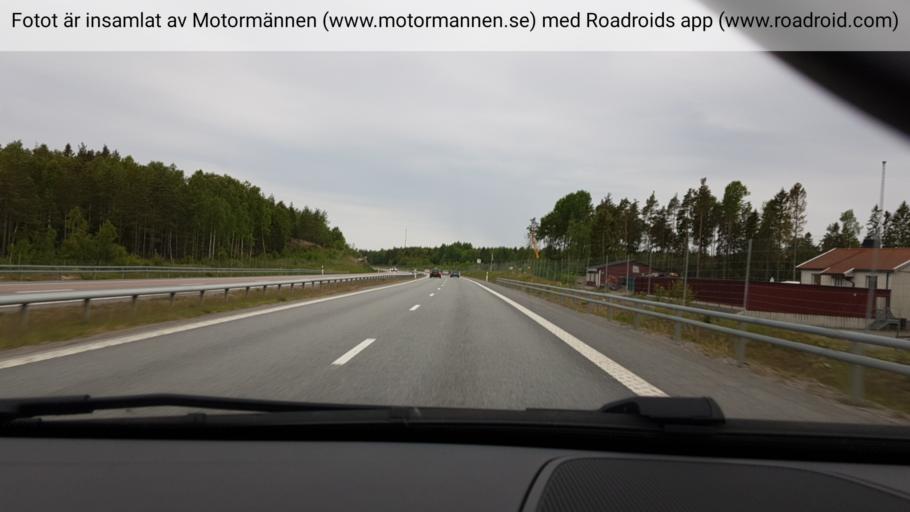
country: SE
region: Stockholm
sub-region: Haninge Kommun
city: Jordbro
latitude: 59.0874
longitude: 18.0851
